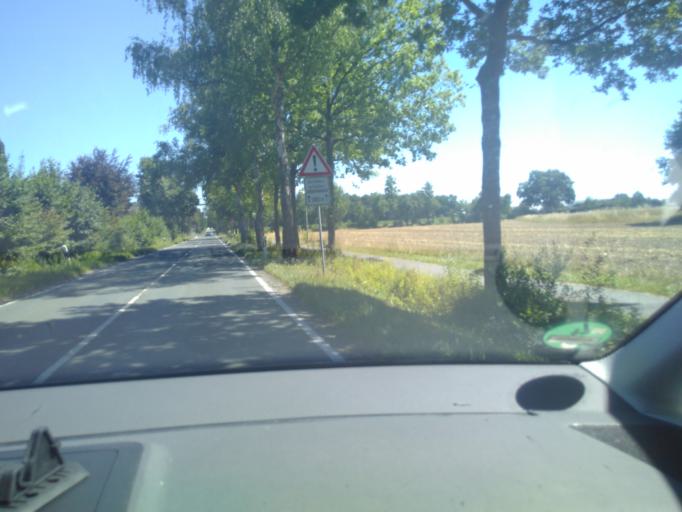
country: DE
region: North Rhine-Westphalia
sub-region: Regierungsbezirk Detmold
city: Guetersloh
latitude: 51.8983
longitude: 8.4453
